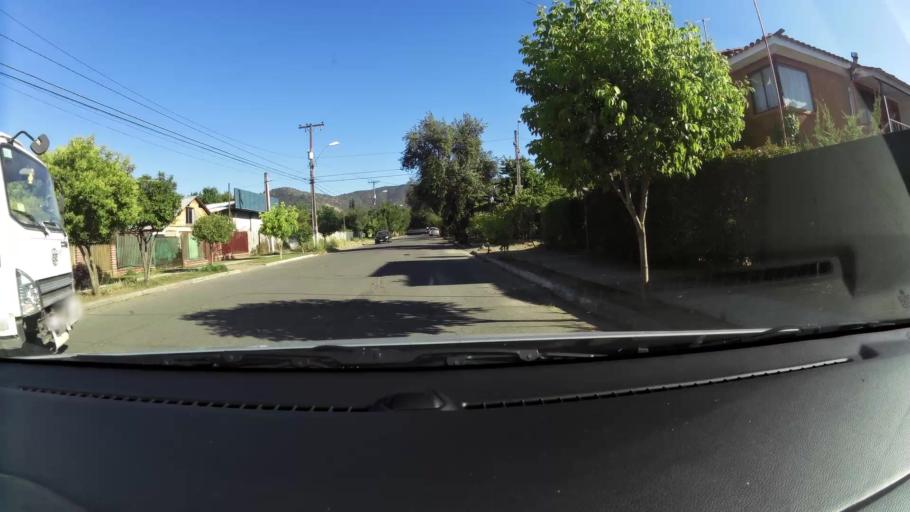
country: CL
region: Santiago Metropolitan
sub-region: Provincia de Chacabuco
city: Lampa
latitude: -33.4004
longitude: -71.1207
